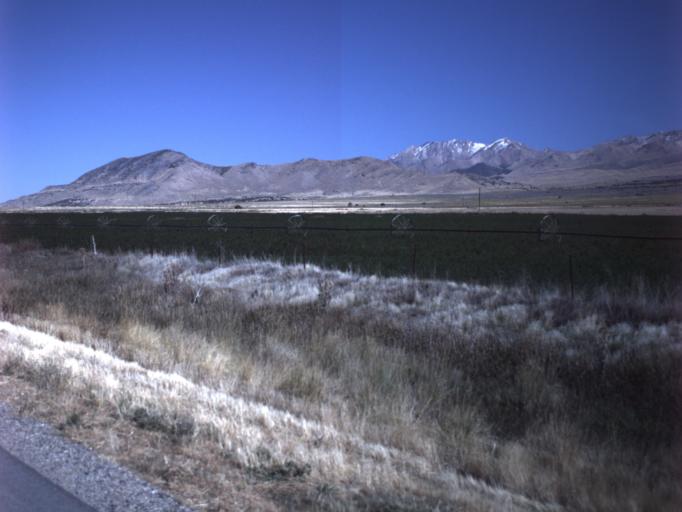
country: US
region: Utah
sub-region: Tooele County
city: Grantsville
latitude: 40.4963
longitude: -112.7480
